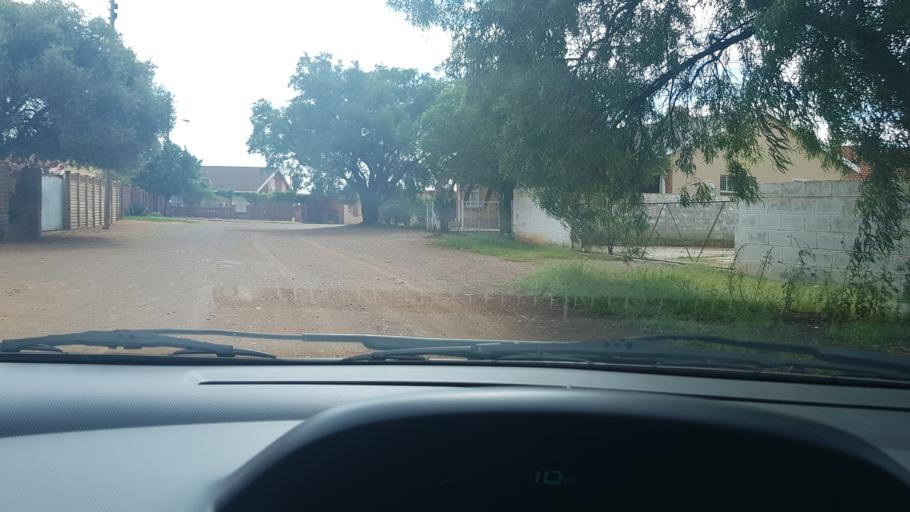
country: ZA
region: Northern Cape
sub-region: Siyanda District Municipality
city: Danielskuil
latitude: -28.1908
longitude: 23.5362
